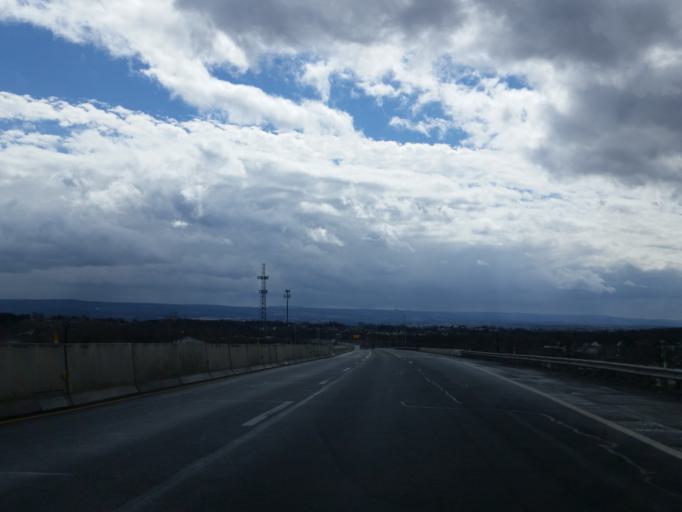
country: US
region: Pennsylvania
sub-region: Lackawanna County
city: Old Forge
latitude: 41.3951
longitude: -75.7316
